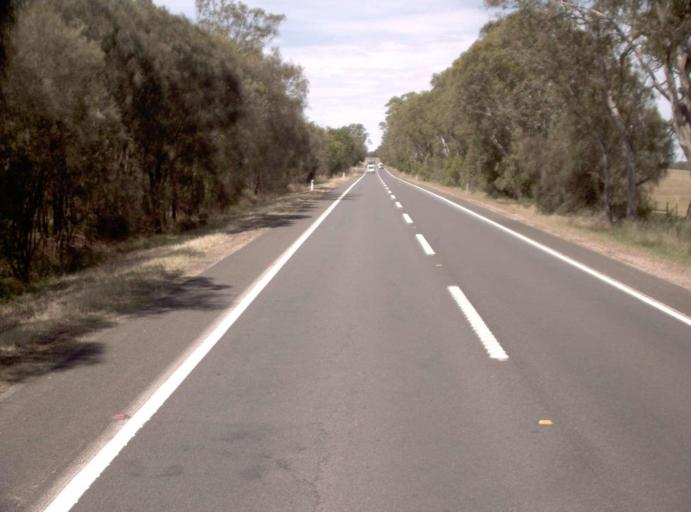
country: AU
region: Victoria
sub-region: Wellington
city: Sale
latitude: -37.9509
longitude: 147.1114
